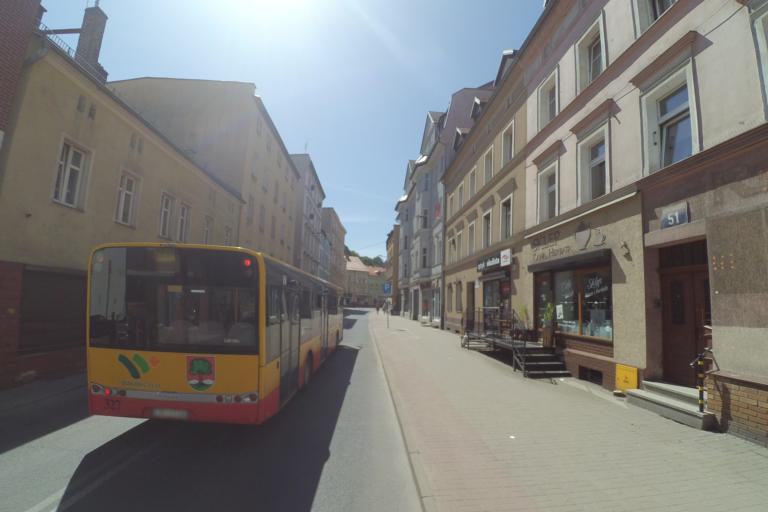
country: PL
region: Lower Silesian Voivodeship
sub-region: Powiat walbrzyski
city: Walbrzych
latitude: 50.7676
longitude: 16.2843
